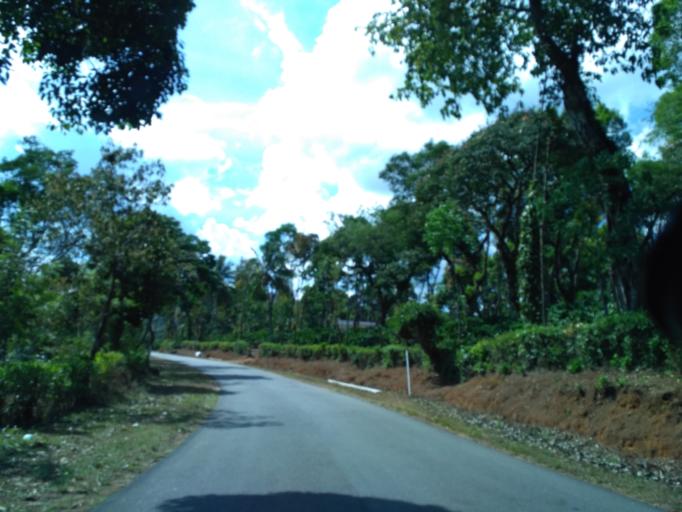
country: IN
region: Karnataka
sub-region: Kodagu
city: Madikeri
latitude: 12.3797
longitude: 75.5835
